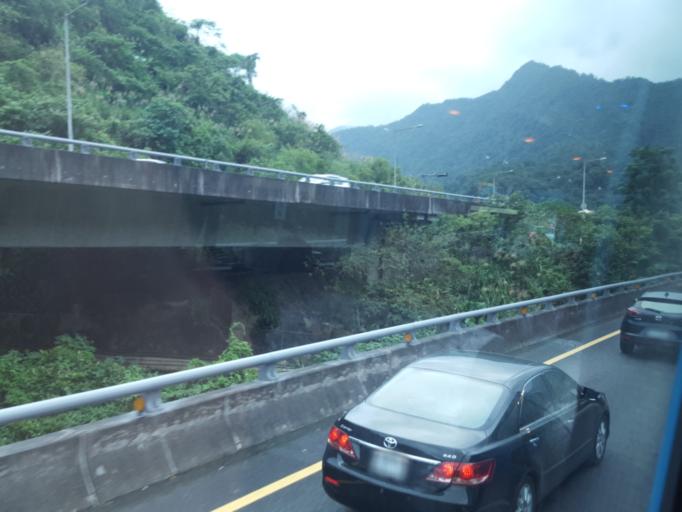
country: TW
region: Taiwan
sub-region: Keelung
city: Keelung
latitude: 24.9443
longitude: 121.7108
